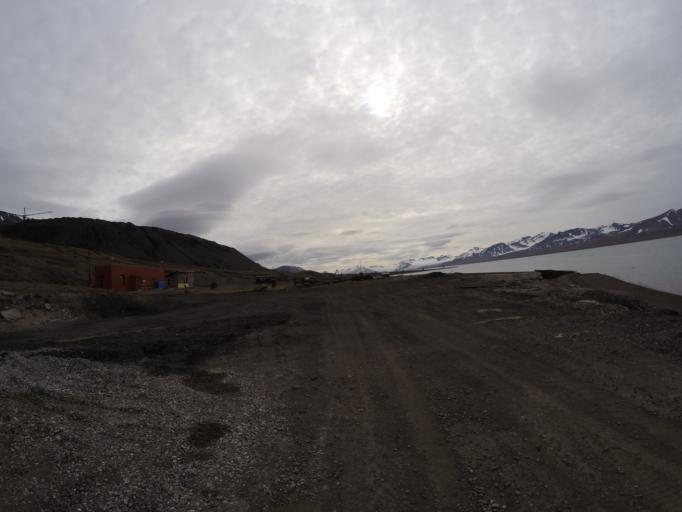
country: SJ
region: Svalbard
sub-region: Spitsbergen
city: Longyearbyen
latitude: 78.0506
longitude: 14.2115
